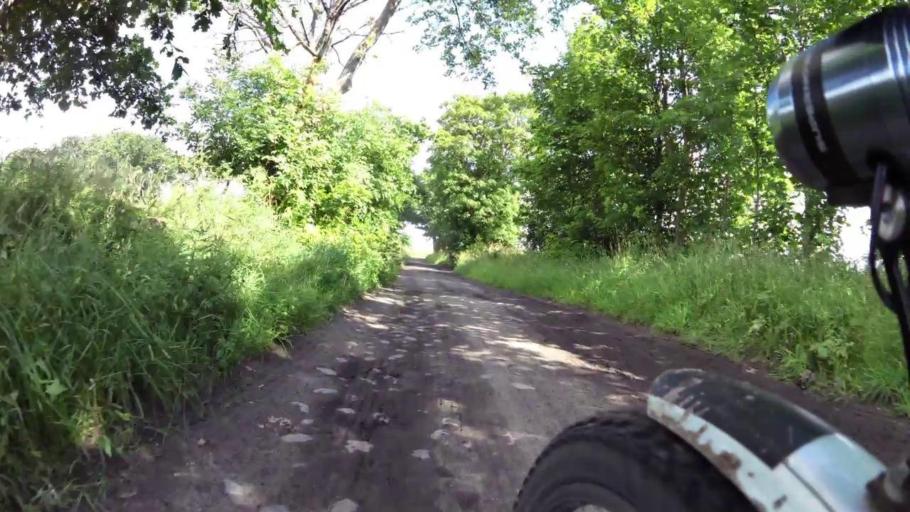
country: PL
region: West Pomeranian Voivodeship
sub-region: Powiat swidwinski
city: Swidwin
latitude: 53.7314
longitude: 15.7433
